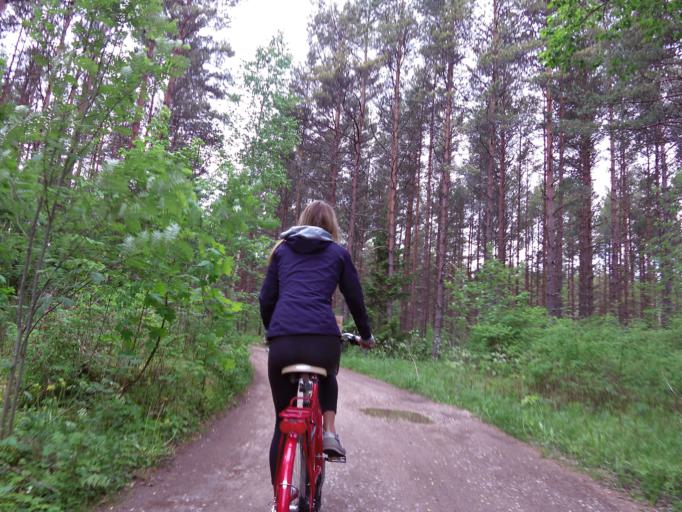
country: EE
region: Harju
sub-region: Paldiski linn
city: Paldiski
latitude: 59.2527
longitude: 23.7530
